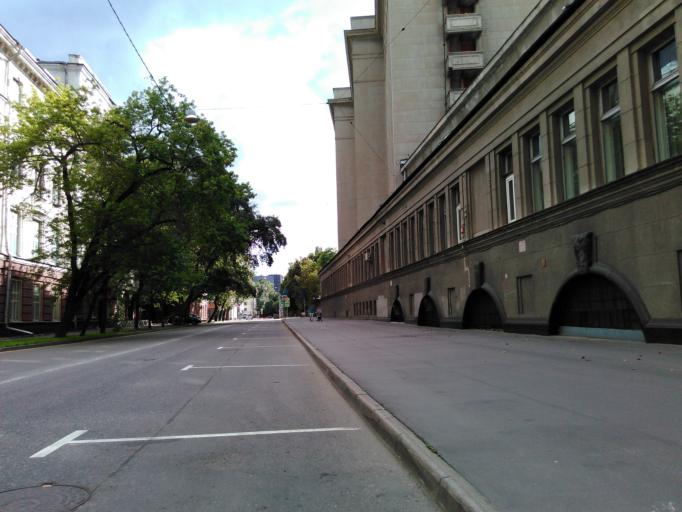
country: RU
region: Moskovskaya
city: Dorogomilovo
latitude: 55.7323
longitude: 37.5752
